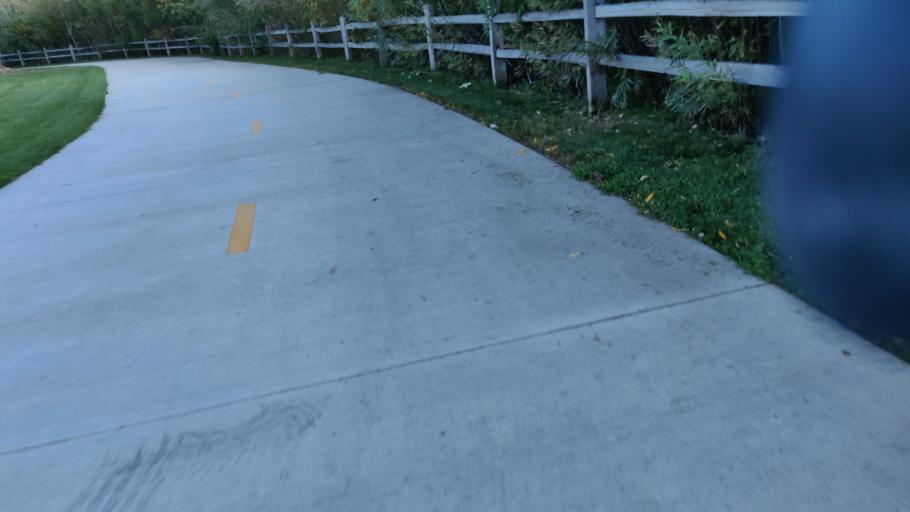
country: US
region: Idaho
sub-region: Ada County
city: Boise
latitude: 43.5716
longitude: -116.1438
